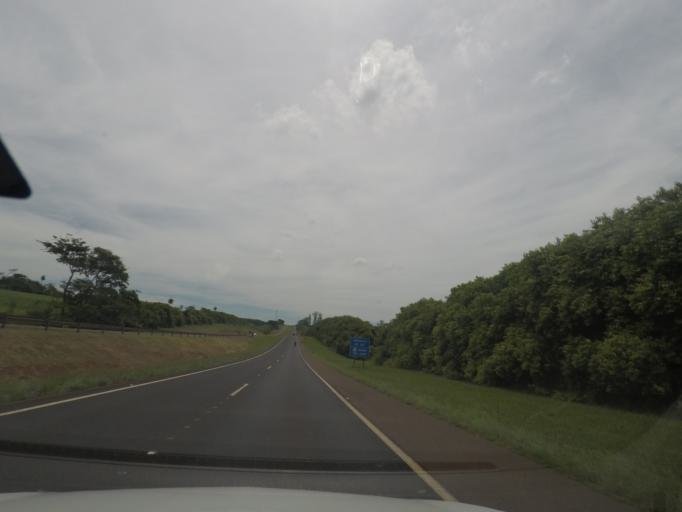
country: BR
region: Sao Paulo
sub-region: Bebedouro
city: Bebedouro
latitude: -21.0026
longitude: -48.4297
